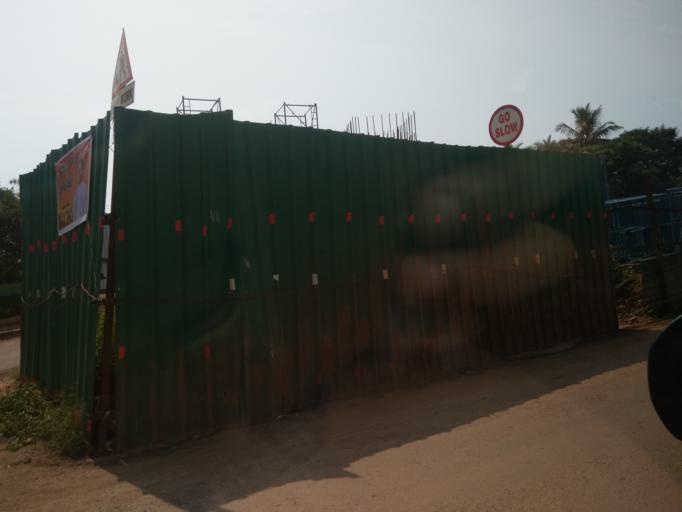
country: IN
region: Goa
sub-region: North Goa
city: Panaji
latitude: 15.4951
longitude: 73.8385
